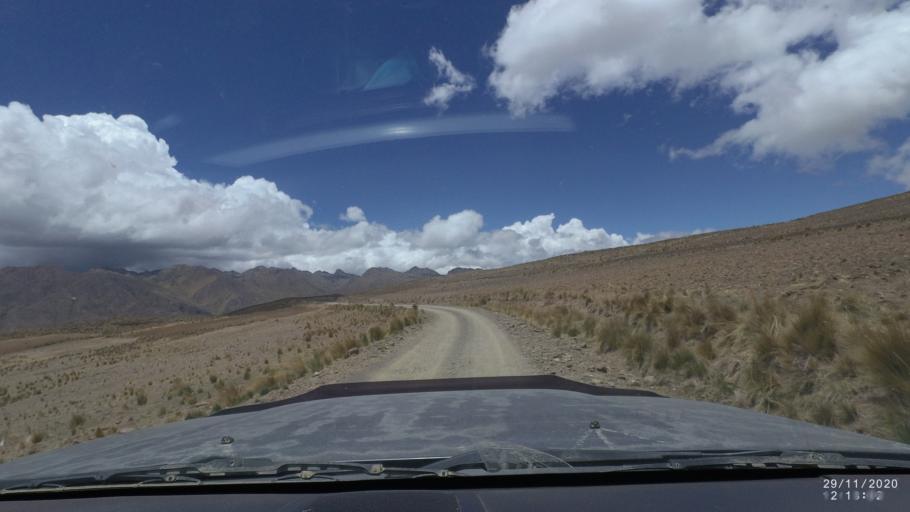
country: BO
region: Cochabamba
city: Cochabamba
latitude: -17.1098
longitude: -66.3045
